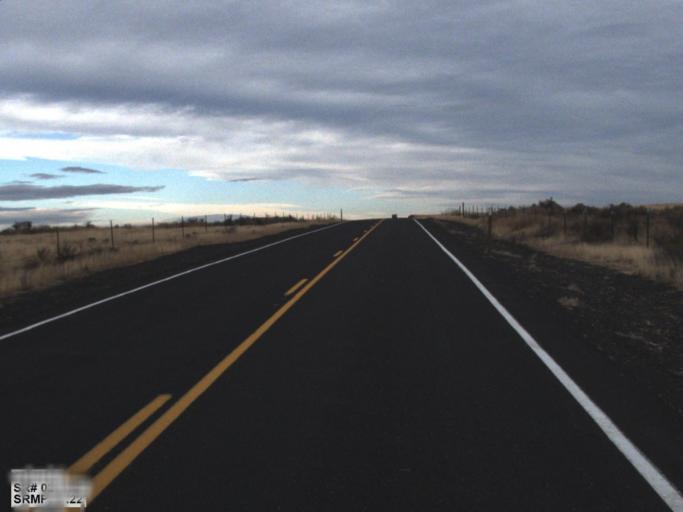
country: US
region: Washington
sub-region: Okanogan County
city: Coulee Dam
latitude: 47.7012
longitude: -118.7221
